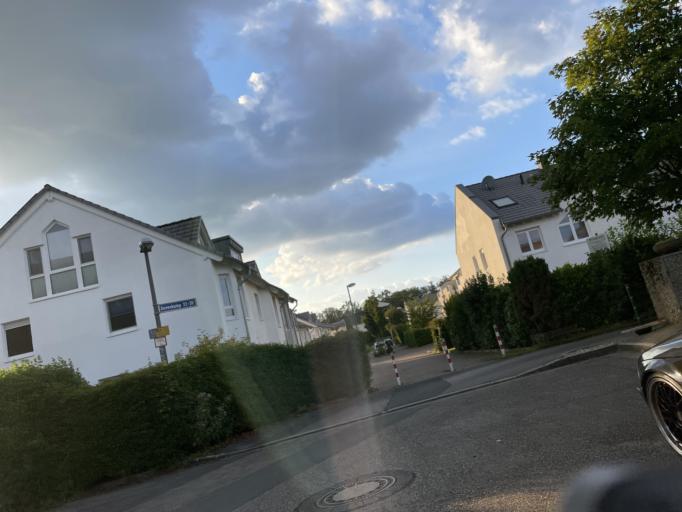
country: DE
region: North Rhine-Westphalia
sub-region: Regierungsbezirk Dusseldorf
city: Essen
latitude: 51.4091
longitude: 7.0535
